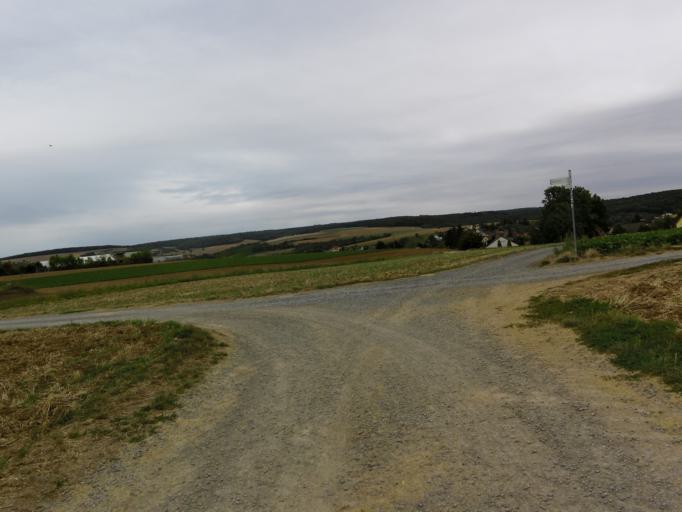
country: DE
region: Bavaria
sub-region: Regierungsbezirk Unterfranken
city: Rimpar
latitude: 49.8419
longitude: 9.9701
